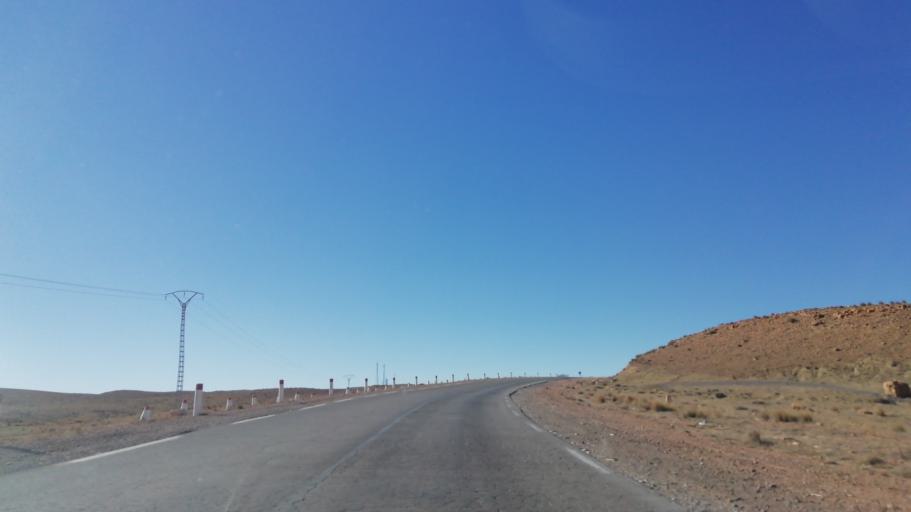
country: DZ
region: El Bayadh
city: El Bayadh
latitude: 33.6666
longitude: 1.4357
